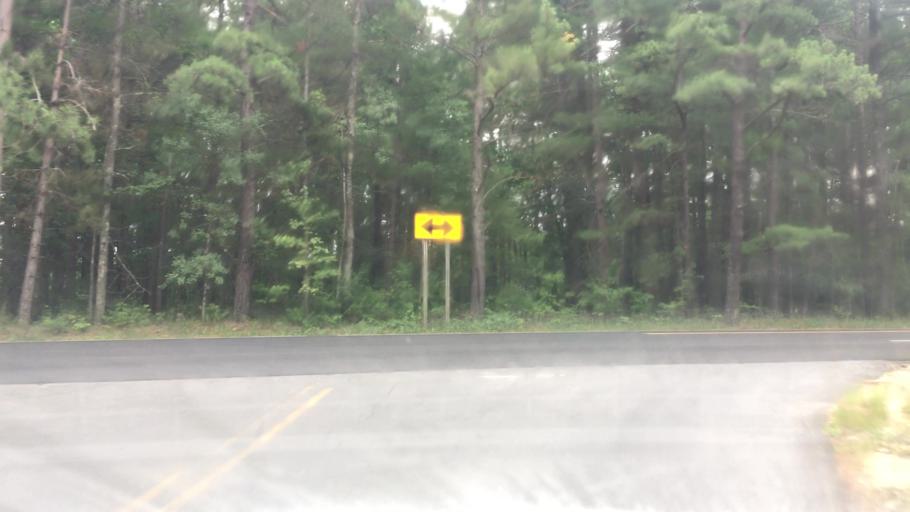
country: US
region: New York
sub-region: Clinton County
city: Morrisonville
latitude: 44.6283
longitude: -73.5846
